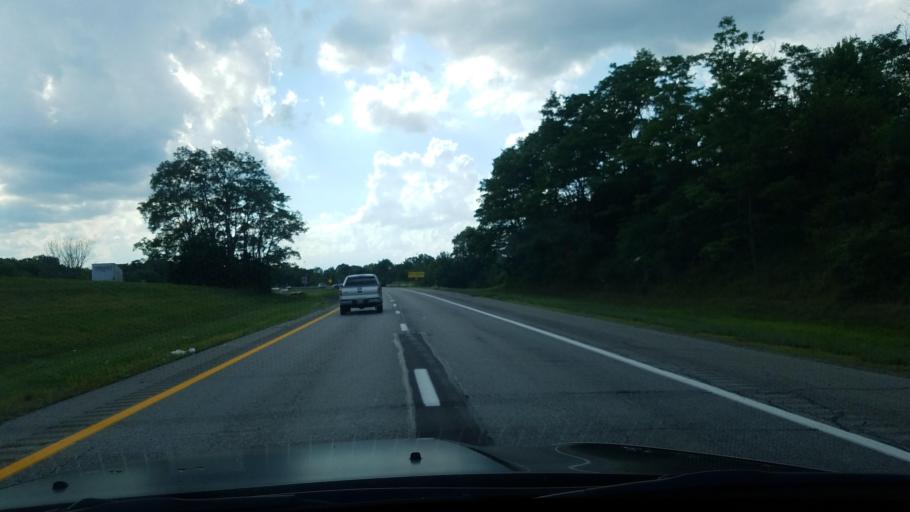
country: US
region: Ohio
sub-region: Trumbull County
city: Mineral Ridge
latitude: 41.1273
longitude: -80.7387
